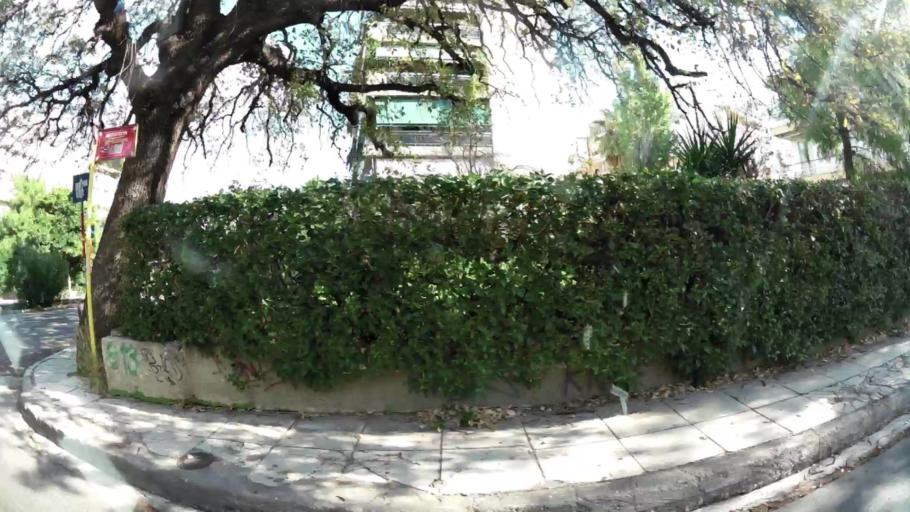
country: GR
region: Attica
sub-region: Nomarchia Athinas
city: Marousi
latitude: 38.0485
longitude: 23.8163
